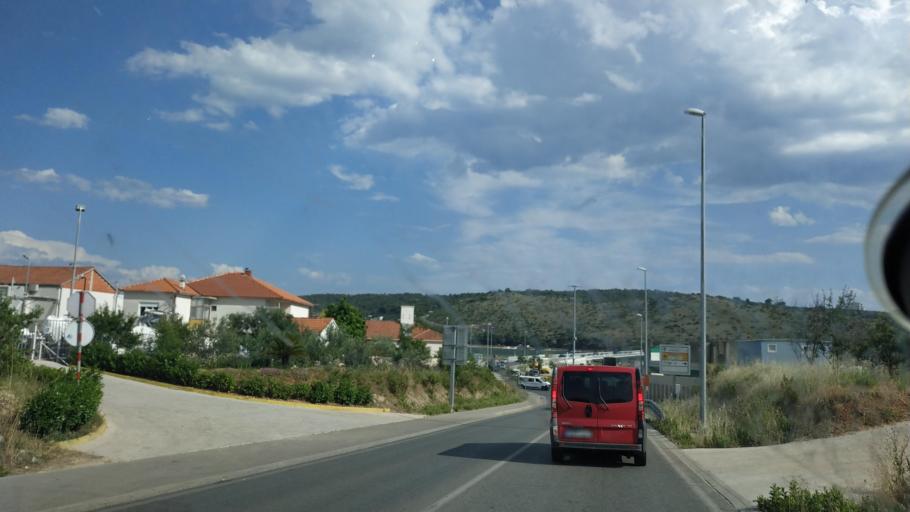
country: HR
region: Splitsko-Dalmatinska
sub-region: Grad Trogir
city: Trogir
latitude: 43.5238
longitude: 16.2638
